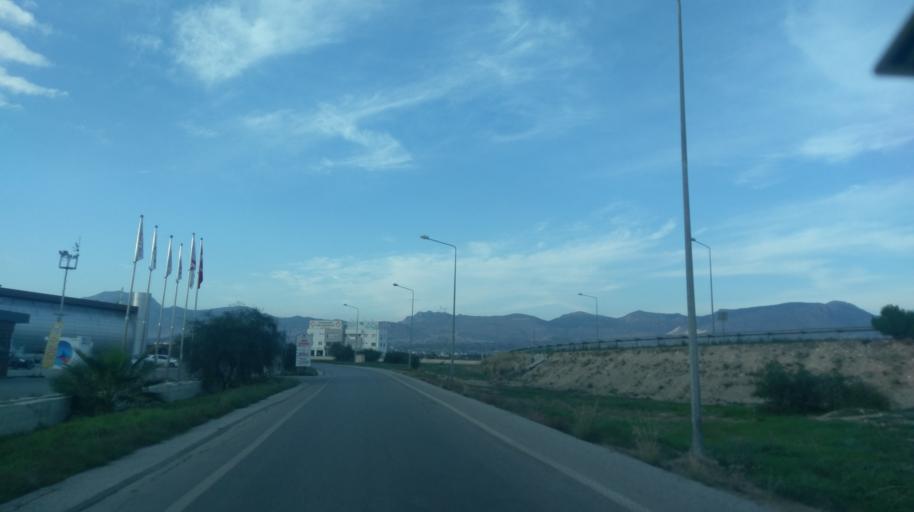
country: CY
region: Lefkosia
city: Geri
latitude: 35.2162
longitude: 33.4982
